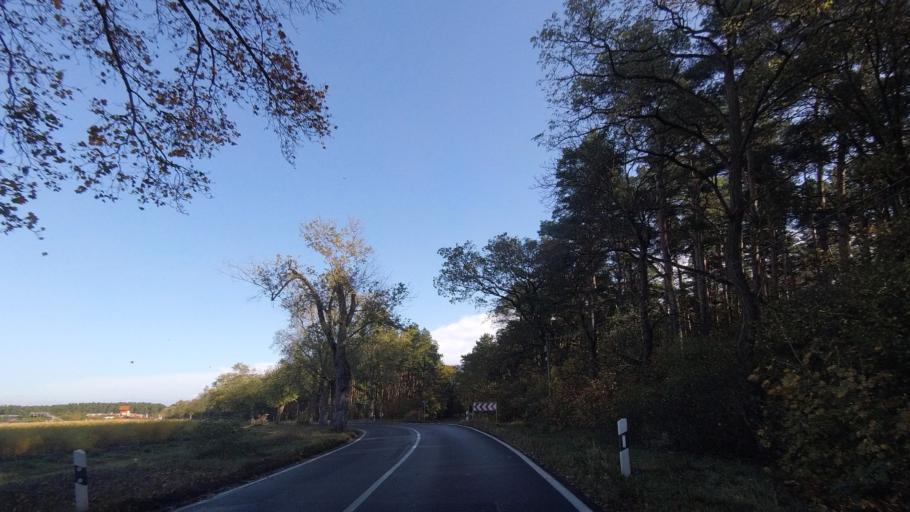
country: DE
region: Brandenburg
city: Fichtenwalde
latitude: 52.2907
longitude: 12.8580
